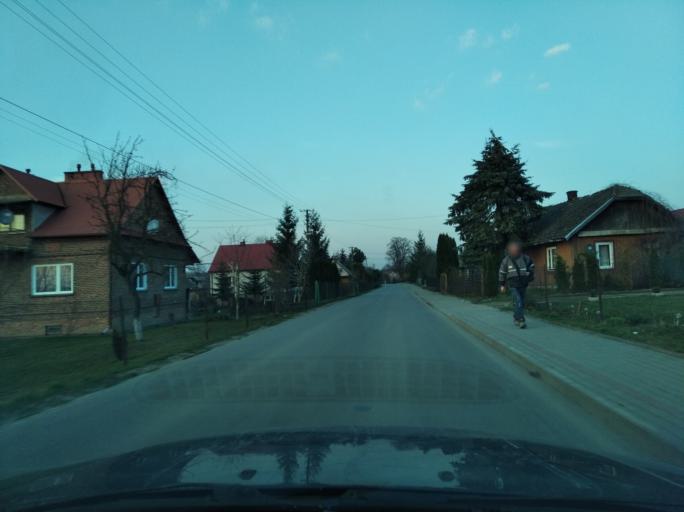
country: PL
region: Subcarpathian Voivodeship
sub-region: Powiat przeworski
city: Zurawiczki
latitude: 50.0249
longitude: 22.5073
